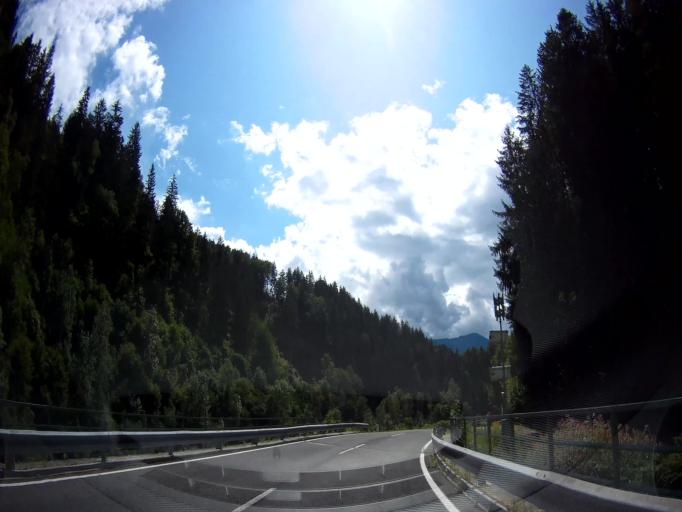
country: AT
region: Carinthia
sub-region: Politischer Bezirk Spittal an der Drau
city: Seeboden
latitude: 46.8408
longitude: 13.5005
